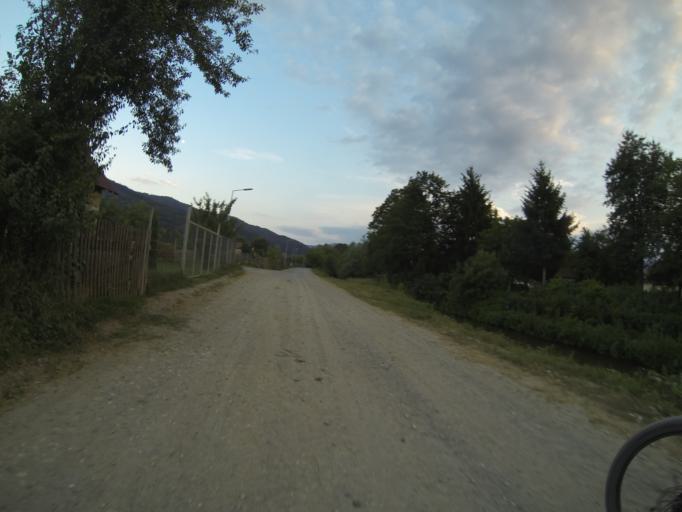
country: RO
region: Brasov
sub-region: Comuna Sinca Noua
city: Sinca Noua
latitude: 45.7084
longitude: 25.2456
